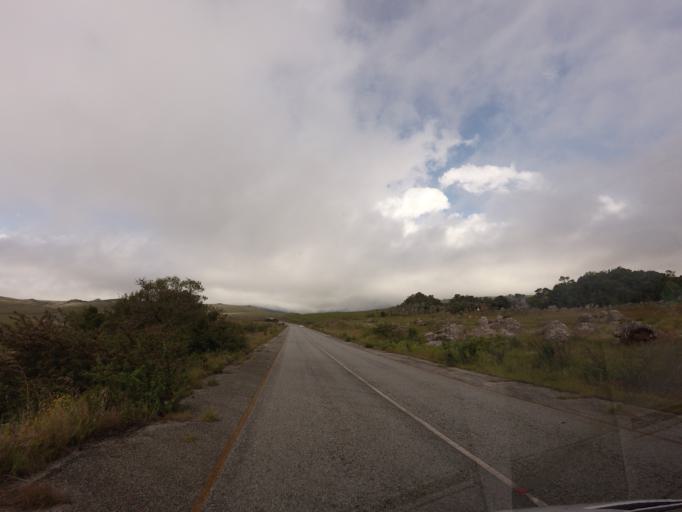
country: ZA
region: Mpumalanga
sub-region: Ehlanzeni District
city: Graksop
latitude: -24.8563
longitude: 30.8833
